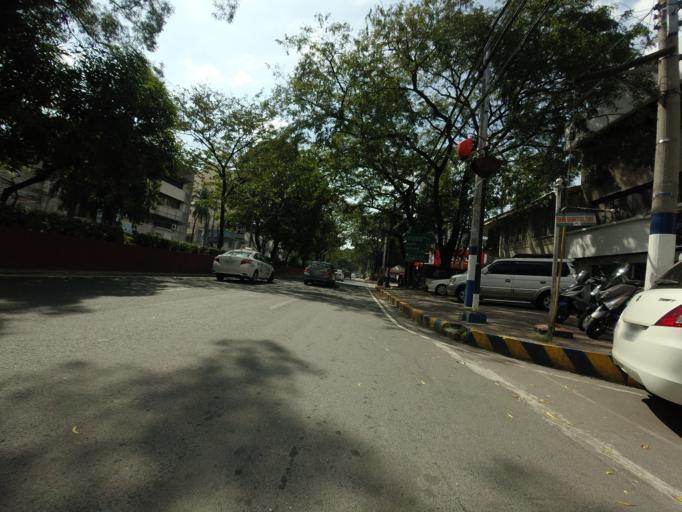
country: PH
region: Metro Manila
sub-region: City of Manila
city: Quiapo
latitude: 14.5732
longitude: 120.9938
